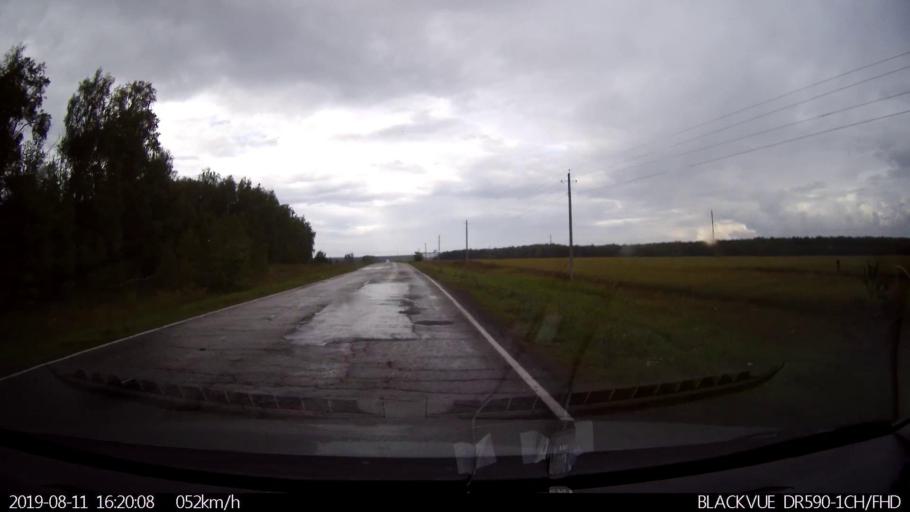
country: RU
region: Ulyanovsk
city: Mayna
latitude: 54.0694
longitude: 47.6043
